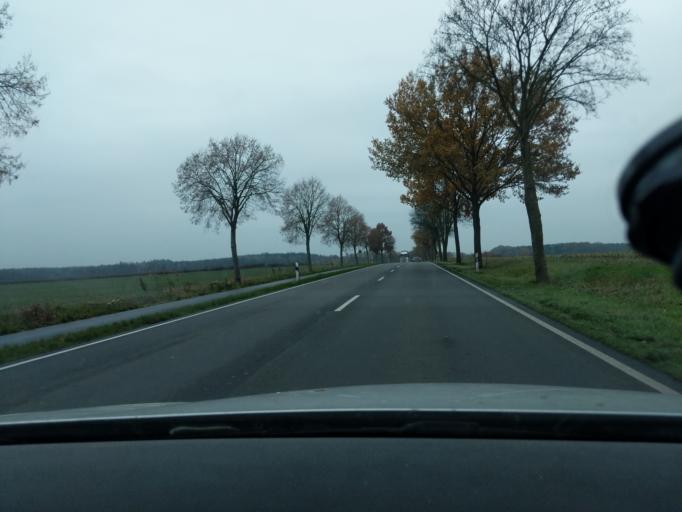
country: DE
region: Lower Saxony
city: Zeven
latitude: 53.2565
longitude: 9.2776
